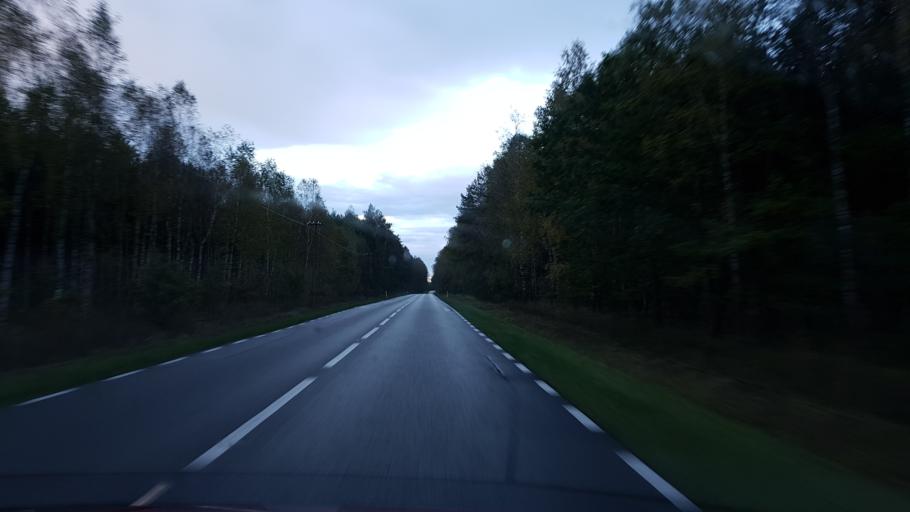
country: PL
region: Greater Poland Voivodeship
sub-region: Powiat zlotowski
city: Krajenka
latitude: 53.2807
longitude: 16.9608
